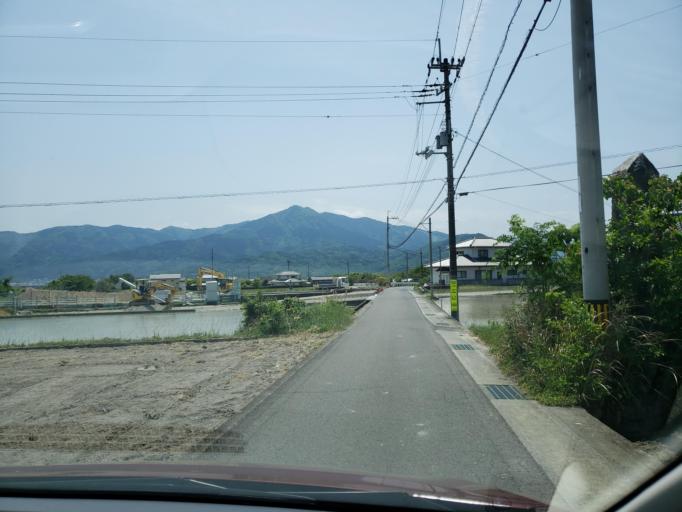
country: JP
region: Tokushima
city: Wakimachi
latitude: 34.0896
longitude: 134.2192
